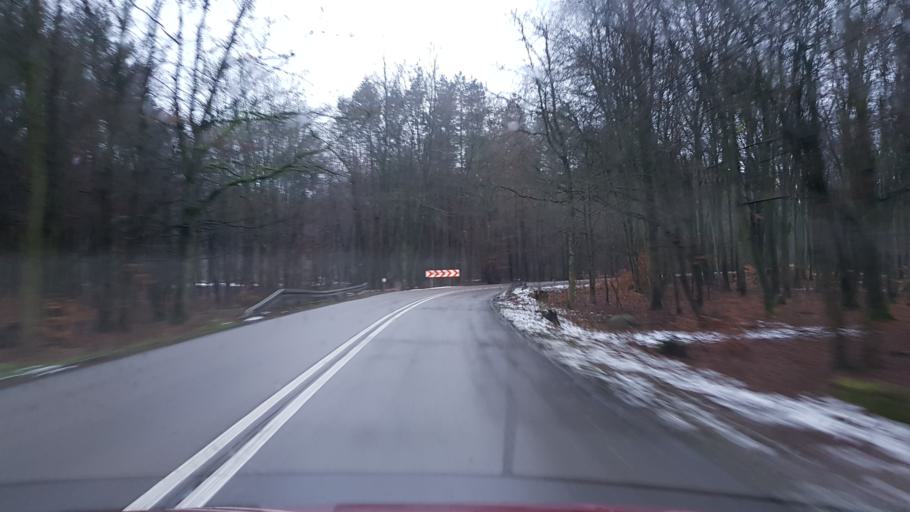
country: PL
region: West Pomeranian Voivodeship
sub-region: Powiat policki
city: Police
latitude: 53.5231
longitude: 14.5263
